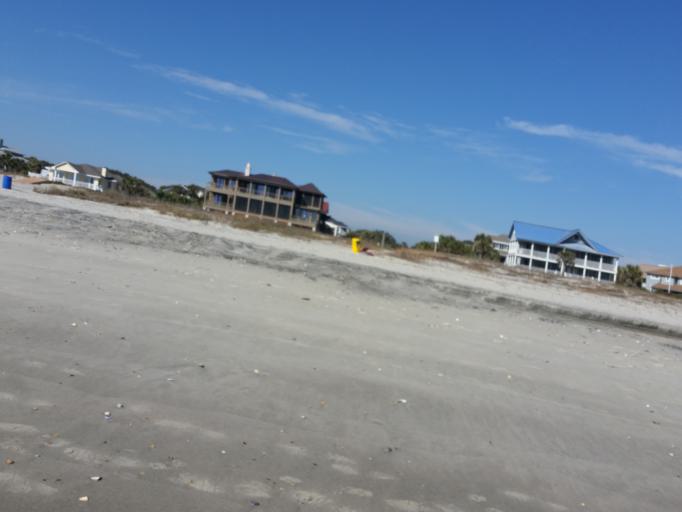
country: US
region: South Carolina
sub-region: Charleston County
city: Isle of Palms
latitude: 32.7969
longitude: -79.7546
